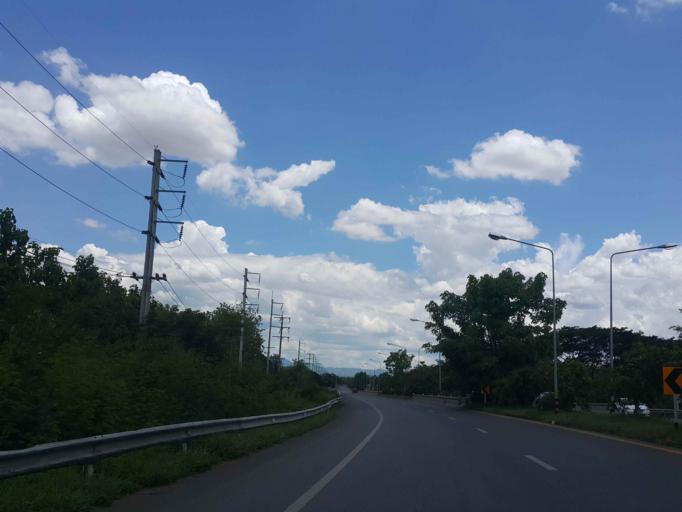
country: TH
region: Phrae
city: Nong Muang Khai
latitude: 18.2201
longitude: 100.1978
